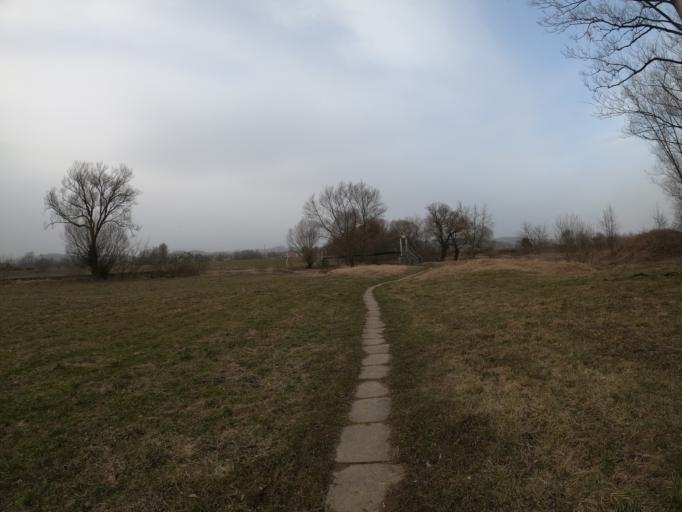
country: PL
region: Subcarpathian Voivodeship
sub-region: Powiat strzyzowski
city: Wisniowa
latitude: 49.8600
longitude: 21.6429
